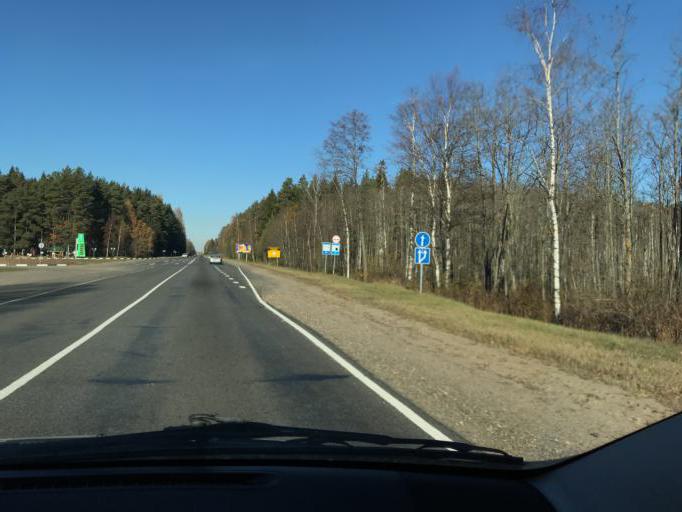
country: BY
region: Vitebsk
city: Polatsk
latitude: 55.4344
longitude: 28.7809
